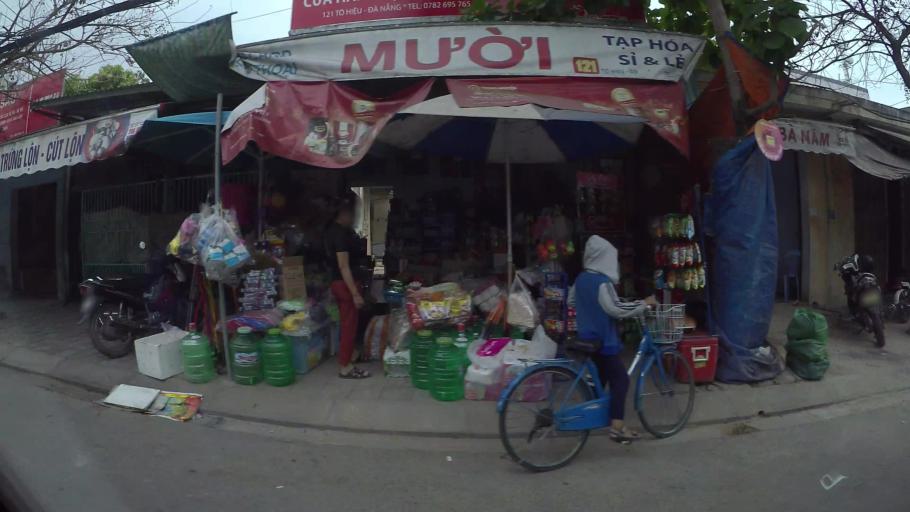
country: VN
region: Da Nang
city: Lien Chieu
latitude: 16.0611
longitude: 108.1671
